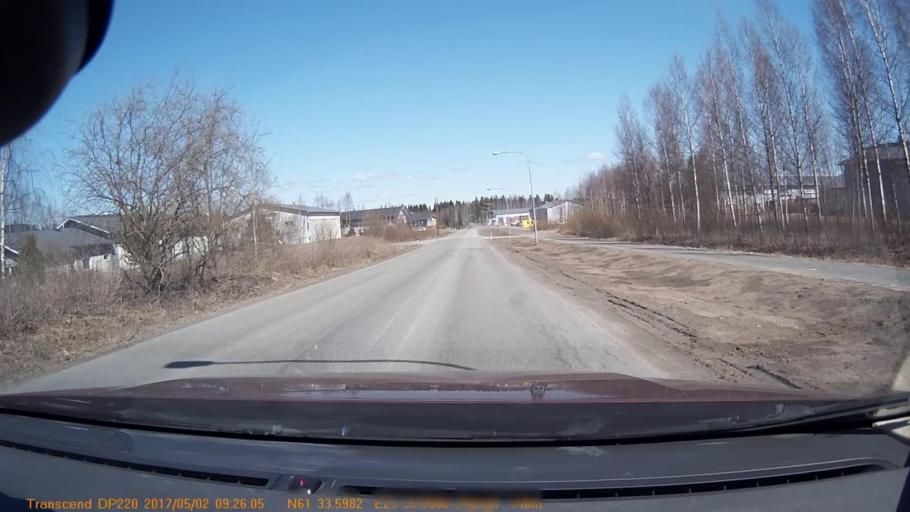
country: FI
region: Pirkanmaa
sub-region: Tampere
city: Yloejaervi
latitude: 61.5599
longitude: 23.5517
